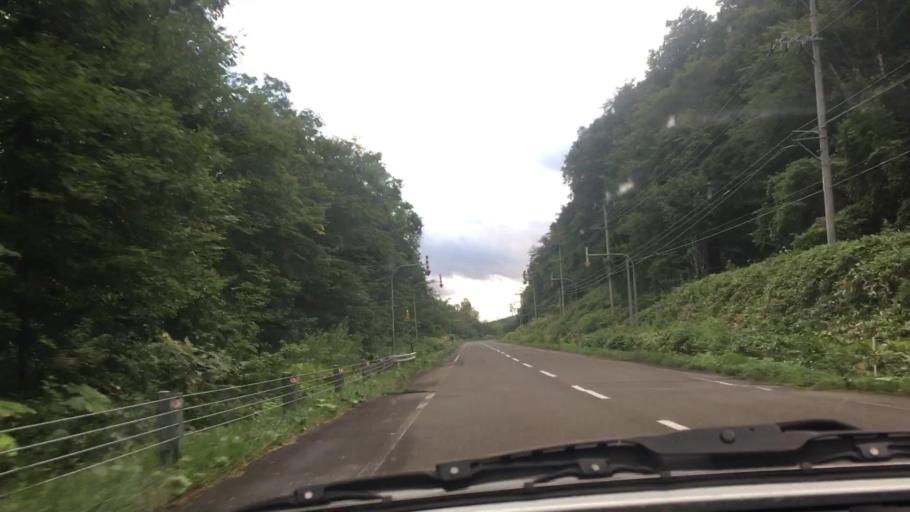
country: JP
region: Hokkaido
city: Shimo-furano
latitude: 43.0186
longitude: 142.4308
